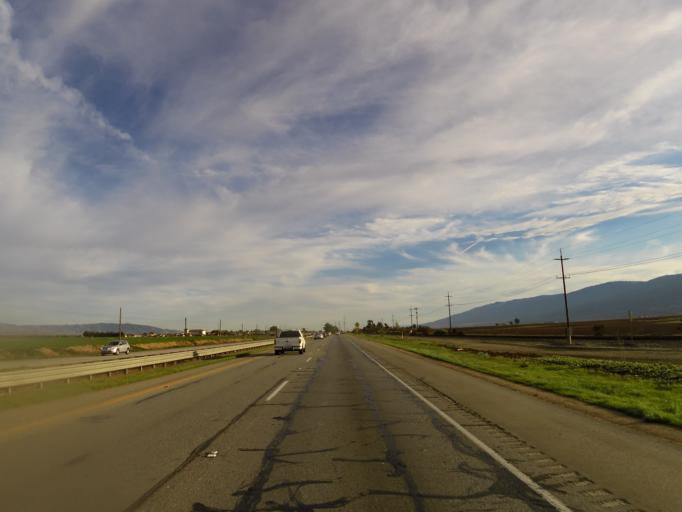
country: US
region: California
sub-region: Monterey County
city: Chualar
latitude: 36.5769
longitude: -121.5264
